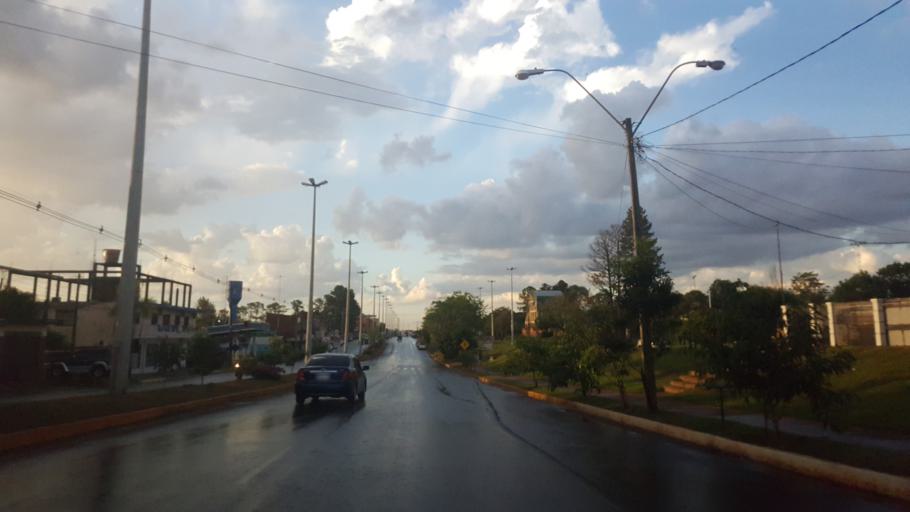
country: PY
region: Itapua
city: Encarnacion
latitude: -27.3595
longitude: -55.8588
